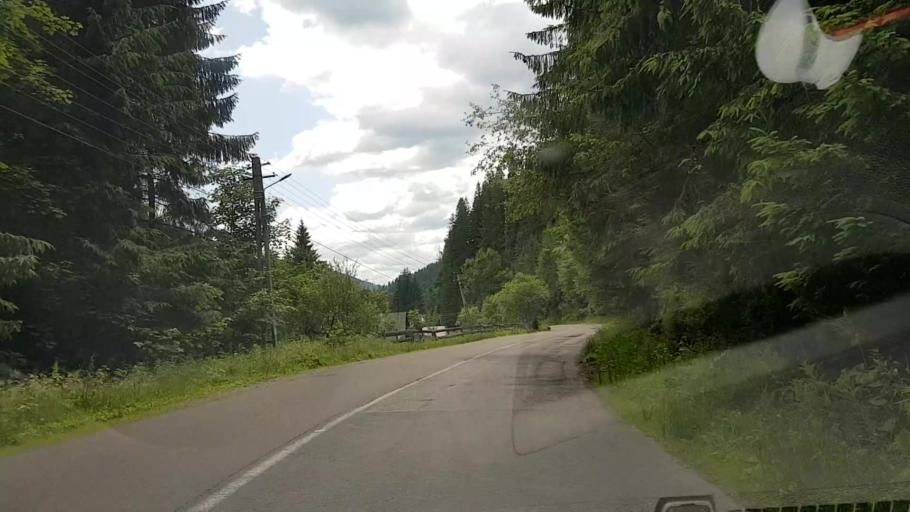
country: RO
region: Suceava
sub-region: Comuna Crucea
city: Crucea
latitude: 47.3492
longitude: 25.6058
